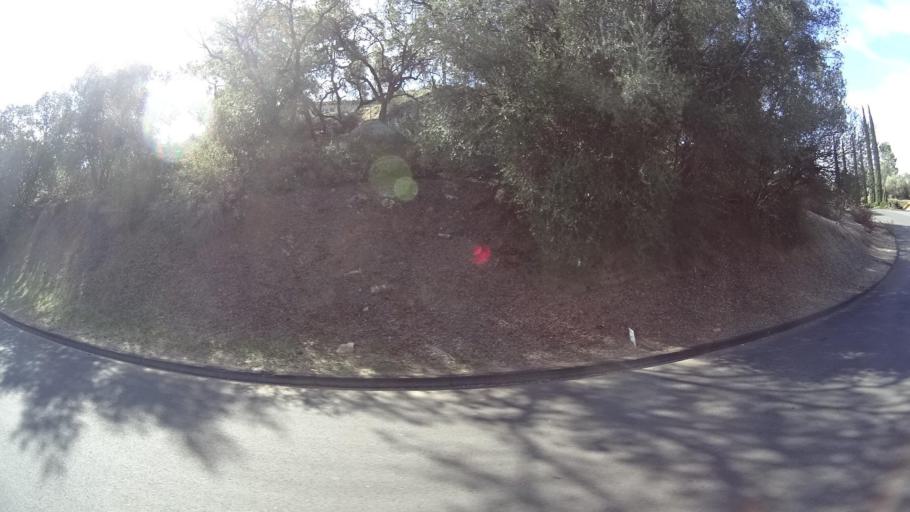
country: US
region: California
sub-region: San Diego County
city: Alpine
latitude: 32.8150
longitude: -116.7734
